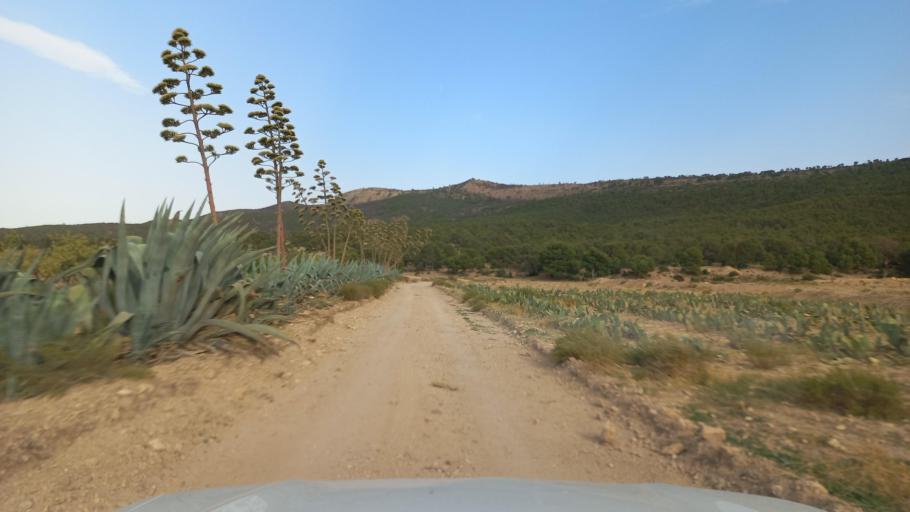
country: TN
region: Al Qasrayn
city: Kasserine
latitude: 35.3337
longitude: 8.8483
